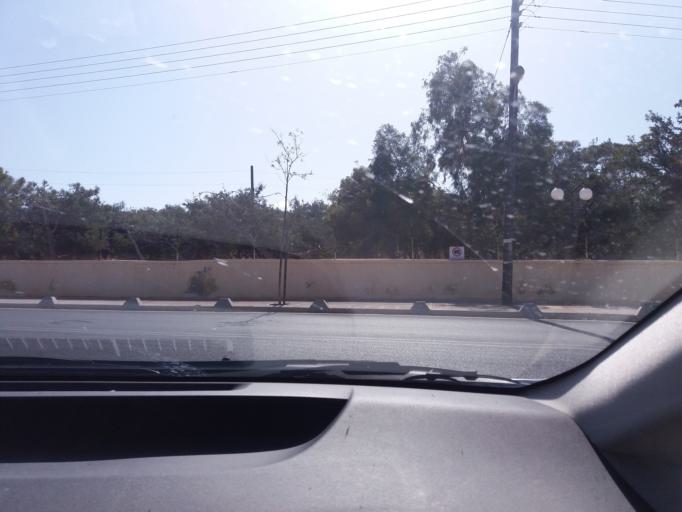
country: GR
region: Crete
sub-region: Nomos Irakleiou
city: Nea Alikarnassos
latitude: 35.3375
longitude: 25.1663
